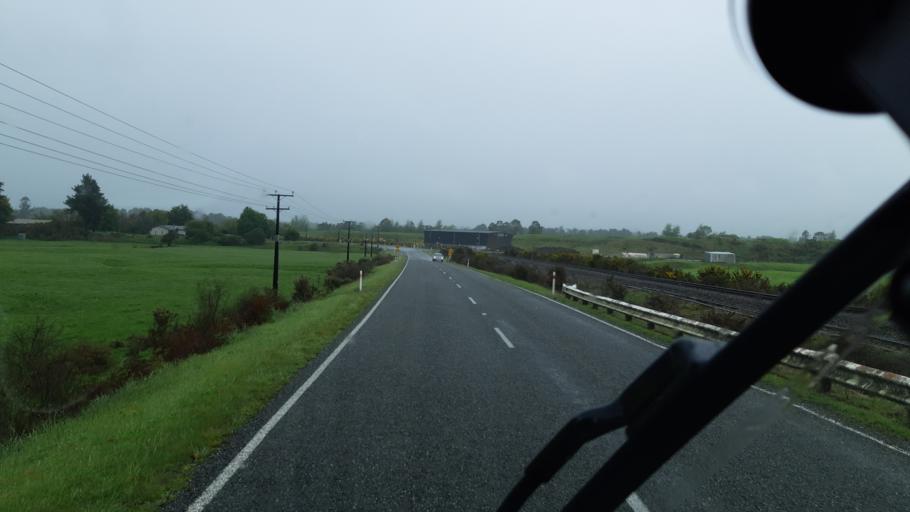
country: NZ
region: West Coast
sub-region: Buller District
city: Westport
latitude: -42.1520
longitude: 171.7567
